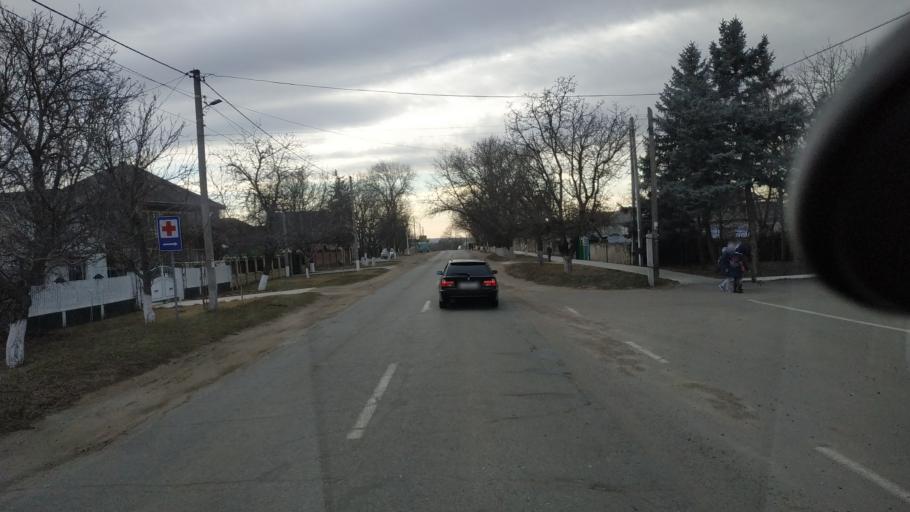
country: MD
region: Criuleni
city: Criuleni
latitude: 47.1663
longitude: 29.1227
